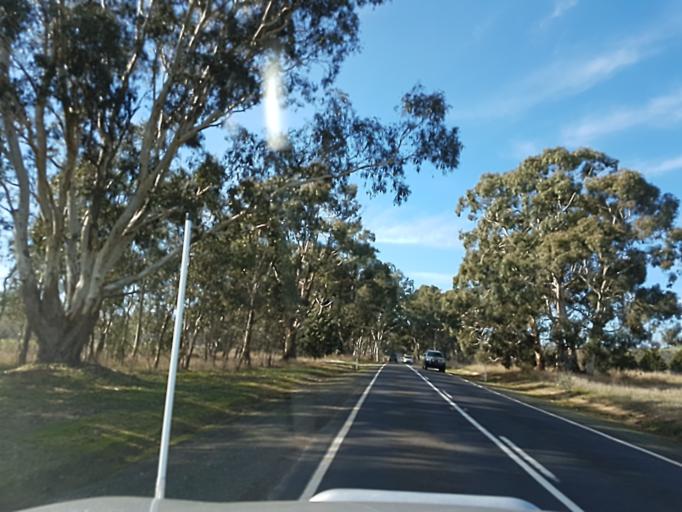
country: AU
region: Victoria
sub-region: Murrindindi
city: Alexandra
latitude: -37.1490
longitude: 145.6065
